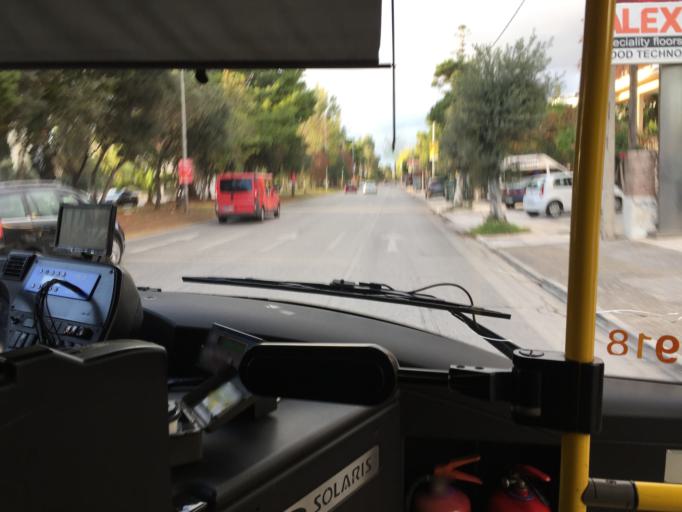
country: GR
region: Attica
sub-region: Nomarchia Athinas
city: Elliniko
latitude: 37.8738
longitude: 23.7349
